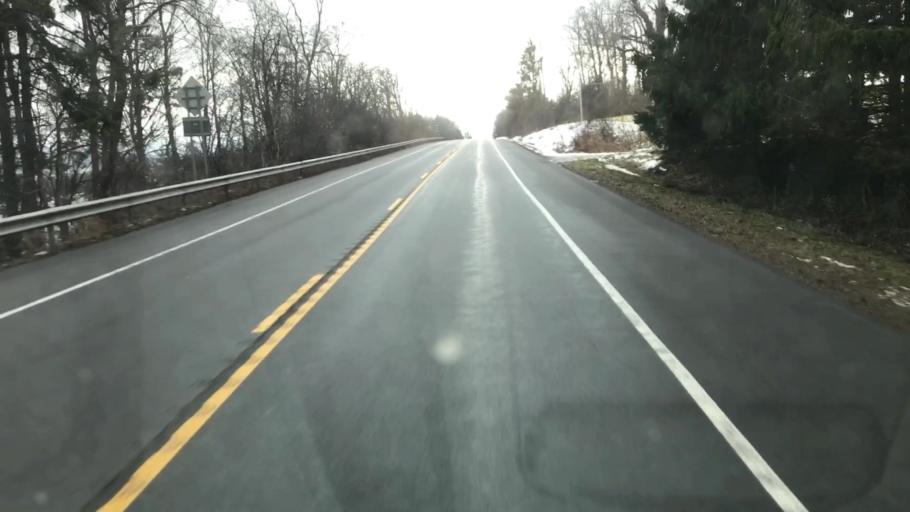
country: US
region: New York
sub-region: Onondaga County
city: Skaneateles
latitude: 42.9077
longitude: -76.4258
